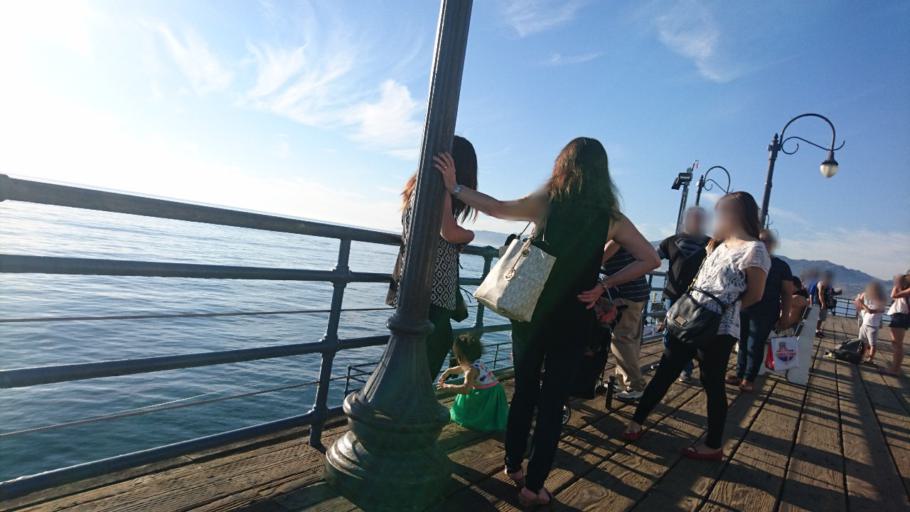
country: US
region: California
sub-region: Los Angeles County
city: Santa Monica
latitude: 34.0074
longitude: -118.4998
